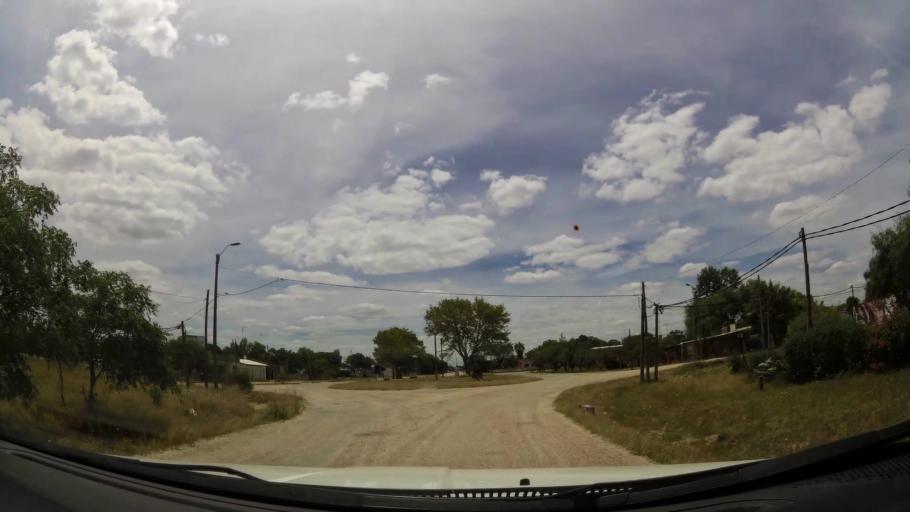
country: UY
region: San Jose
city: Delta del Tigre
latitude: -34.7750
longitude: -56.3736
